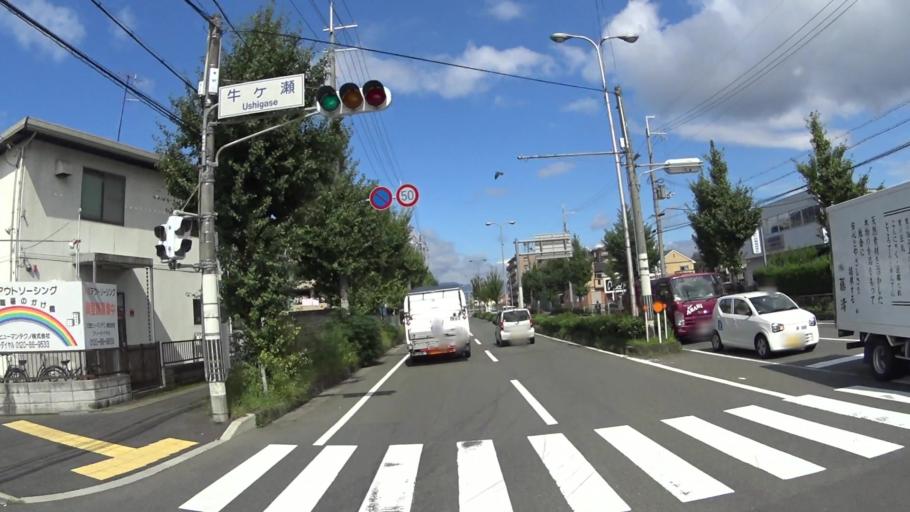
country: JP
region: Kyoto
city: Muko
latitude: 34.9703
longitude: 135.7169
